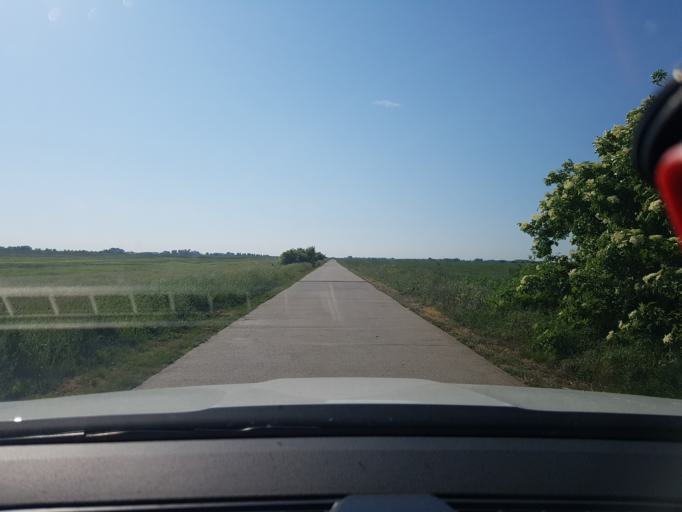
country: HU
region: Tolna
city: Decs
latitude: 46.2812
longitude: 18.7018
